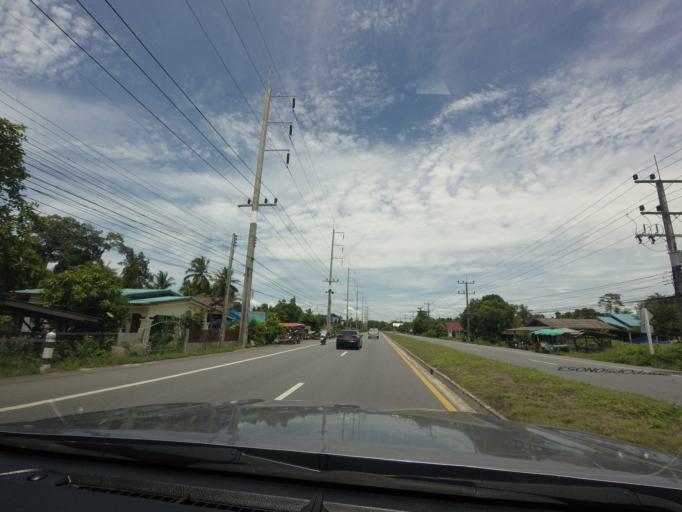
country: TH
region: Songkhla
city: Krasae Sin
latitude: 7.5913
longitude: 100.4043
